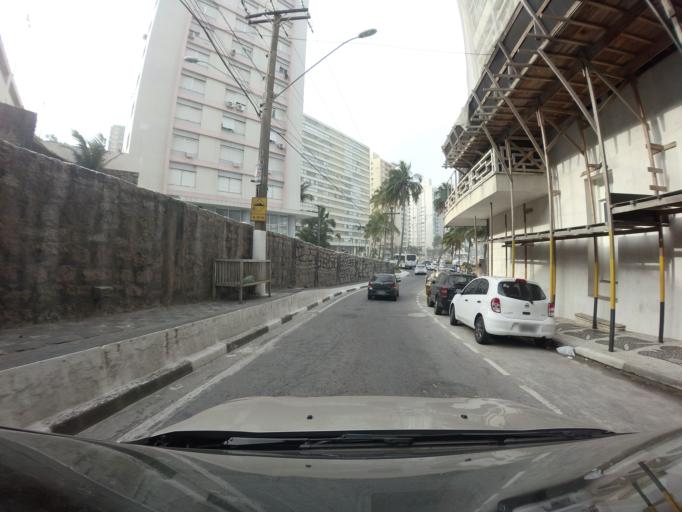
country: BR
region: Sao Paulo
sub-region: Guaruja
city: Guaruja
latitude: -24.0032
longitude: -46.2663
